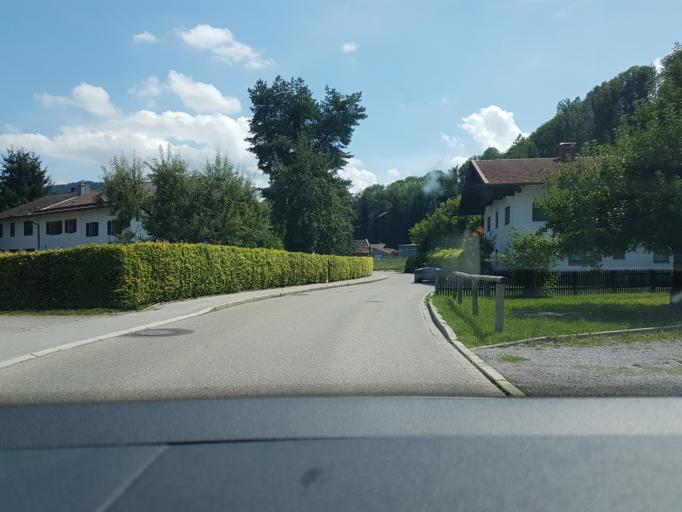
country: DE
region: Bavaria
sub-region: Upper Bavaria
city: Altenmarkt
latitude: 47.7805
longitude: 12.1376
